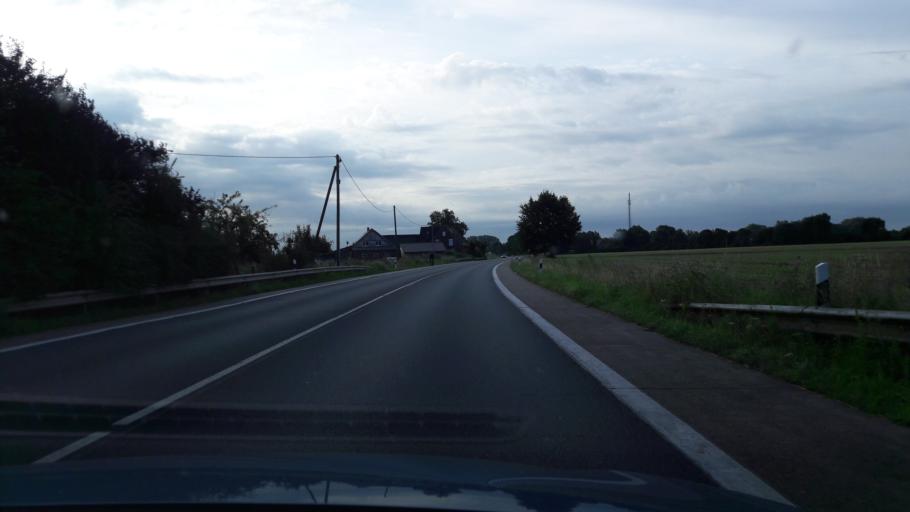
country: DE
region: North Rhine-Westphalia
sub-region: Regierungsbezirk Munster
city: Muenster
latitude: 51.9434
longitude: 7.6978
